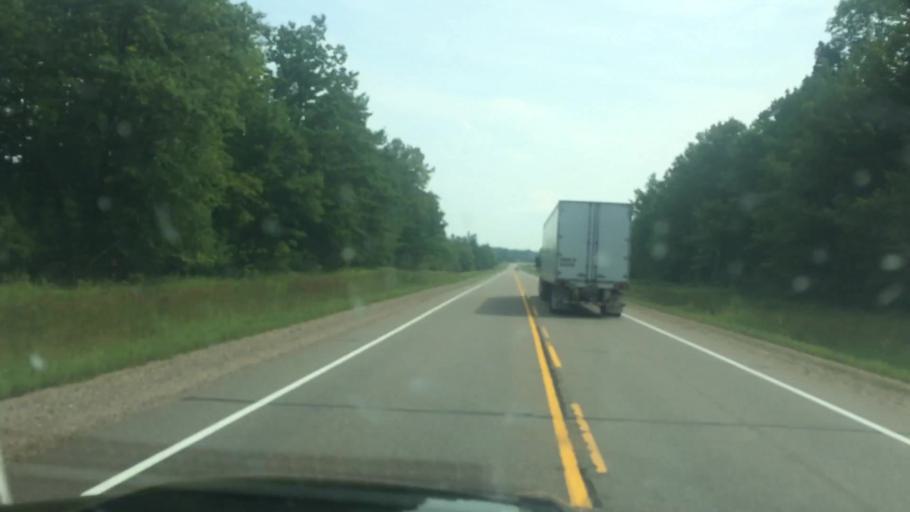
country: US
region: Wisconsin
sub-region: Langlade County
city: Antigo
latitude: 45.1444
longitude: -89.2945
